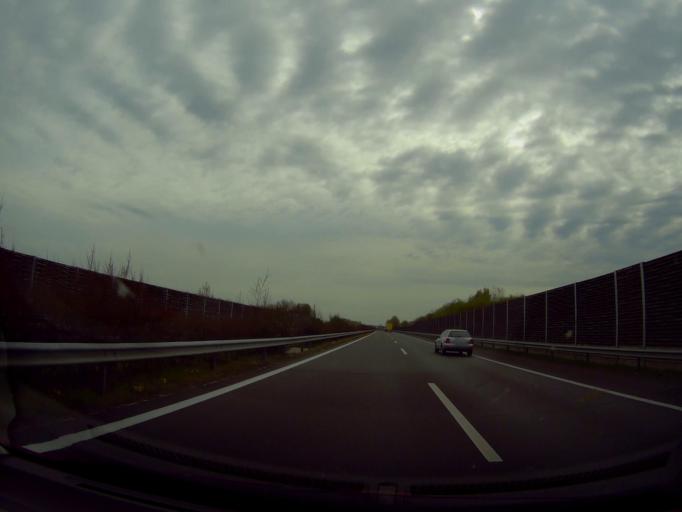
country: HU
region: Csongrad
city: Szatymaz
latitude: 46.3372
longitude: 20.0195
